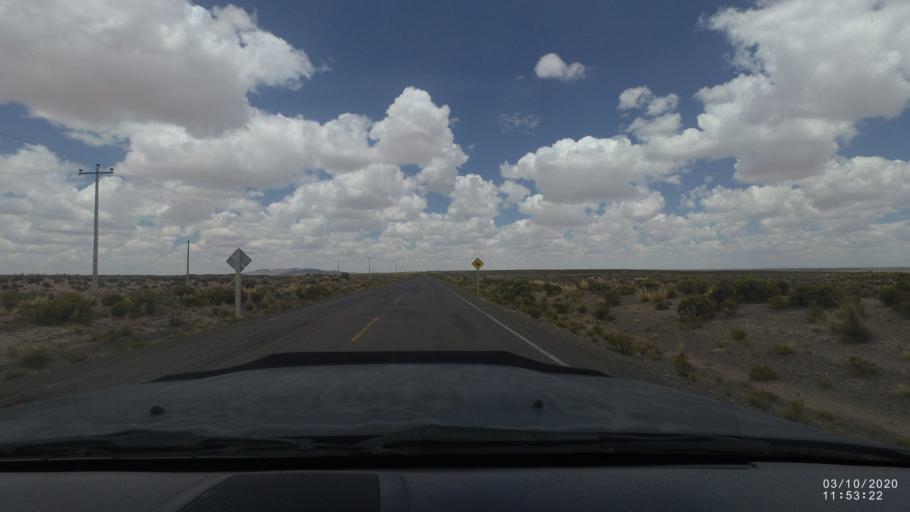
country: BO
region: Oruro
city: Poopo
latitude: -18.4766
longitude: -67.6037
